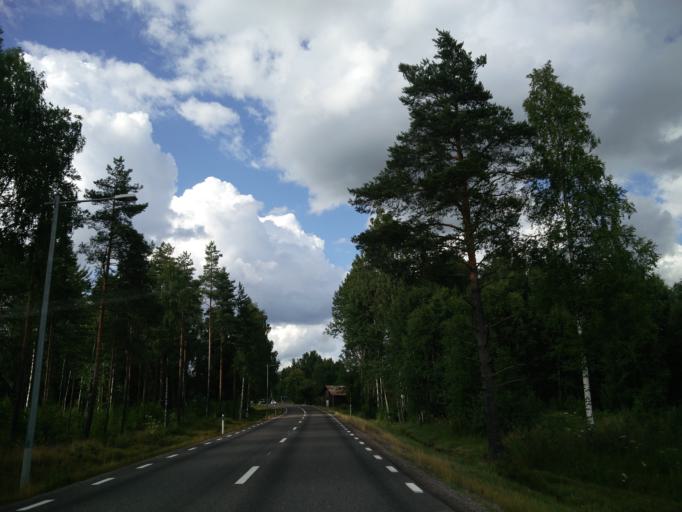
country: SE
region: Vaermland
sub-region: Torsby Kommun
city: Torsby
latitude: 60.2191
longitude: 13.0167
